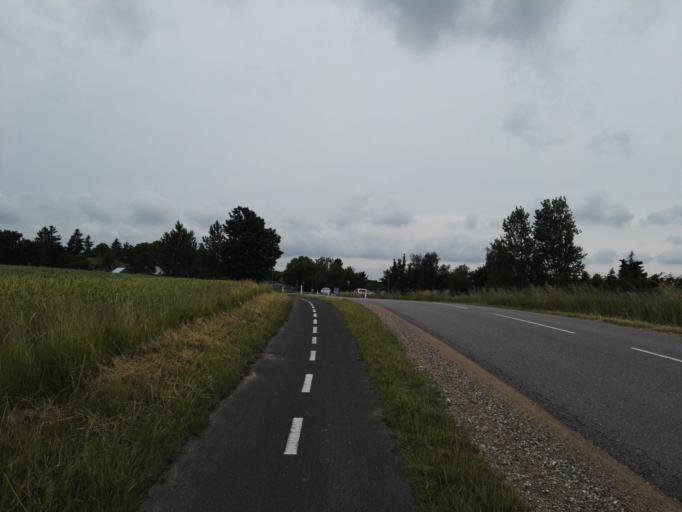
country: DK
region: Capital Region
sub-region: Egedal Kommune
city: Vekso
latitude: 55.7295
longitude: 12.2385
